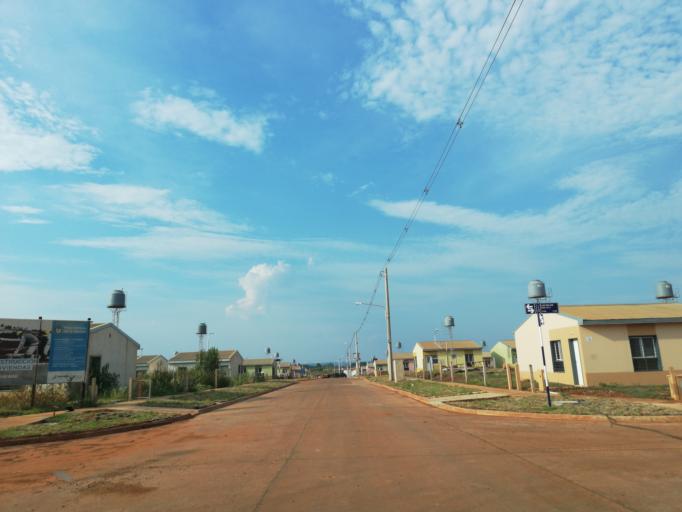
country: AR
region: Misiones
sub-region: Departamento de Capital
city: Posadas
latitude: -27.4005
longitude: -55.9907
